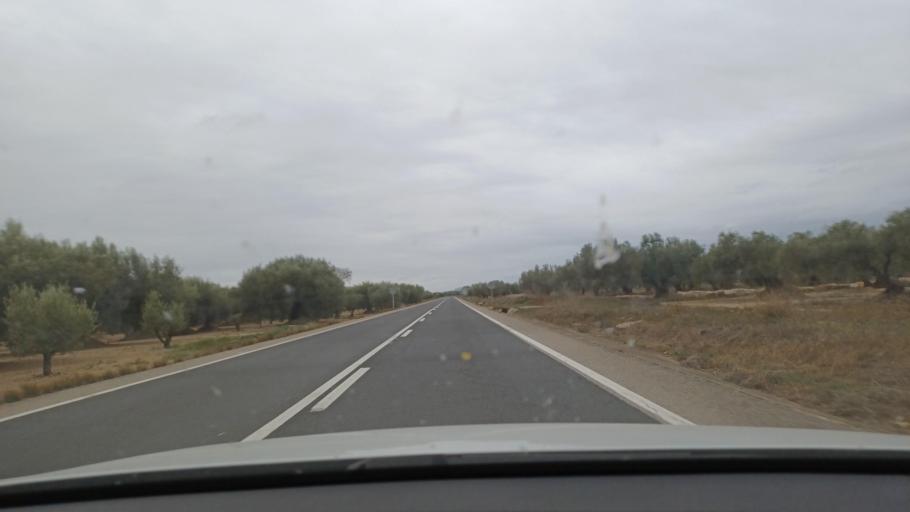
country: ES
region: Catalonia
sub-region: Provincia de Tarragona
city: Ulldecona
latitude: 40.6468
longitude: 0.3849
